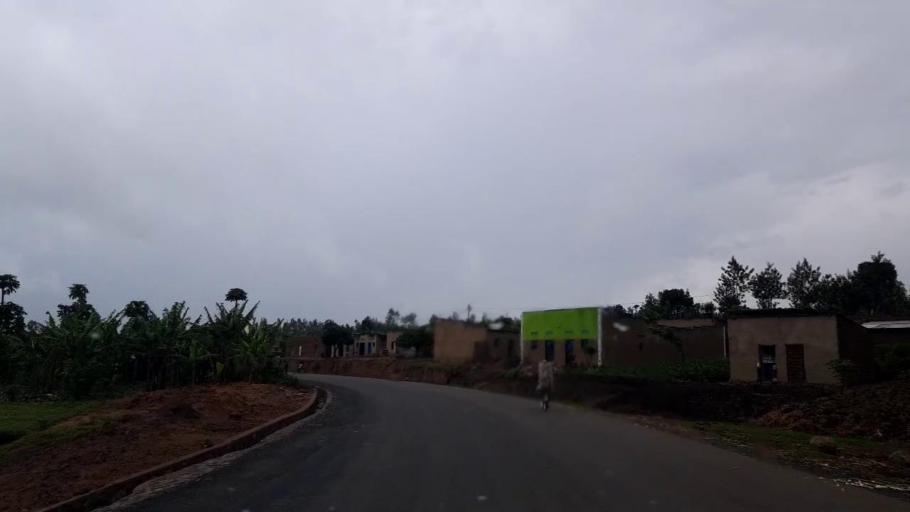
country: RW
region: Northern Province
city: Byumba
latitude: -1.4283
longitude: 30.2754
